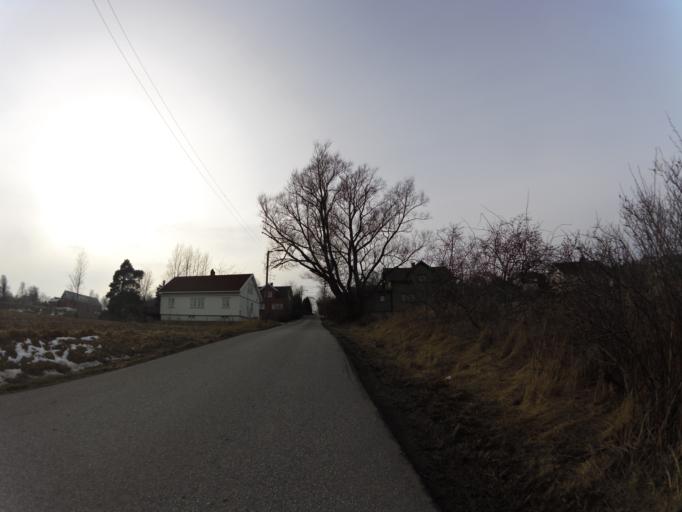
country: NO
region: Ostfold
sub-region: Sarpsborg
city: Sarpsborg
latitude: 59.2725
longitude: 11.0133
